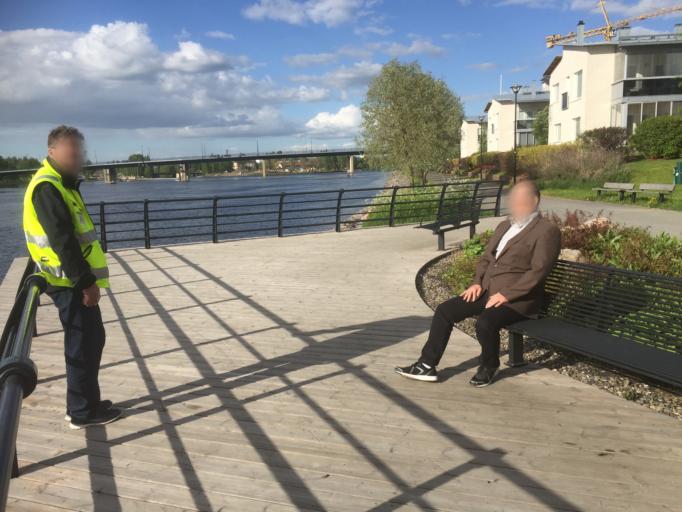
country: FI
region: North Karelia
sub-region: Joensuu
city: Joensuu
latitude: 62.5943
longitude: 29.7629
